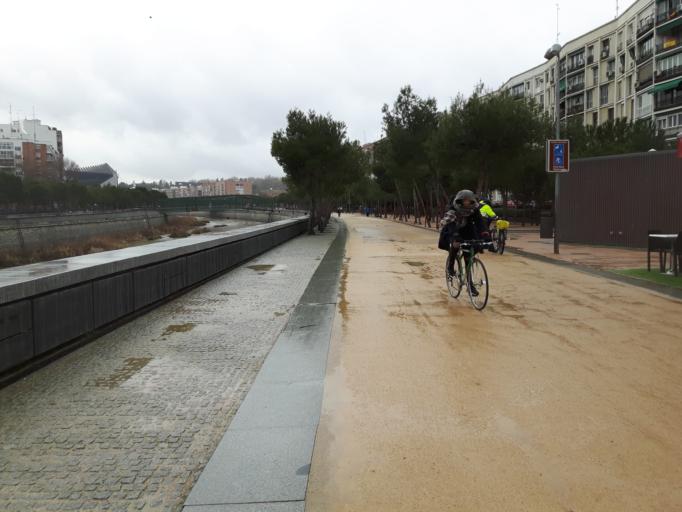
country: ES
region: Madrid
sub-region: Provincia de Madrid
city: Carabanchel
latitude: 40.4072
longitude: -3.7225
